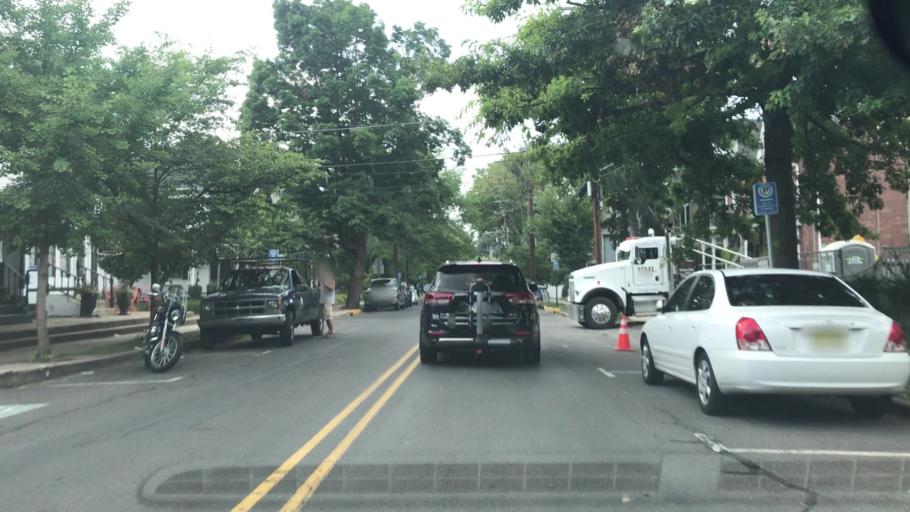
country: US
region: Pennsylvania
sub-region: Bucks County
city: New Hope
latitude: 40.3657
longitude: -74.9519
